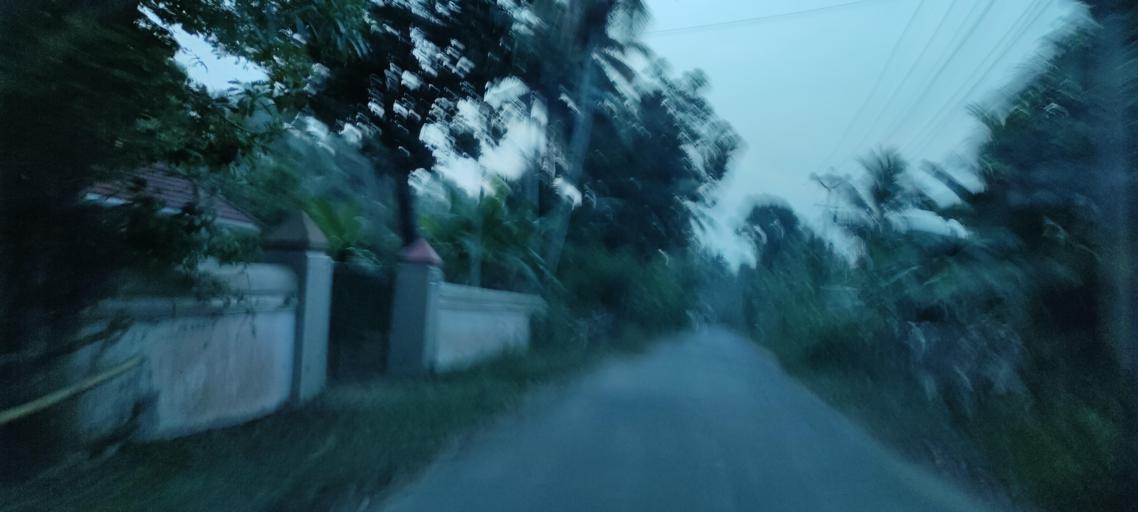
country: IN
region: Kerala
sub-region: Alappuzha
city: Mavelikara
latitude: 9.3308
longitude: 76.4864
